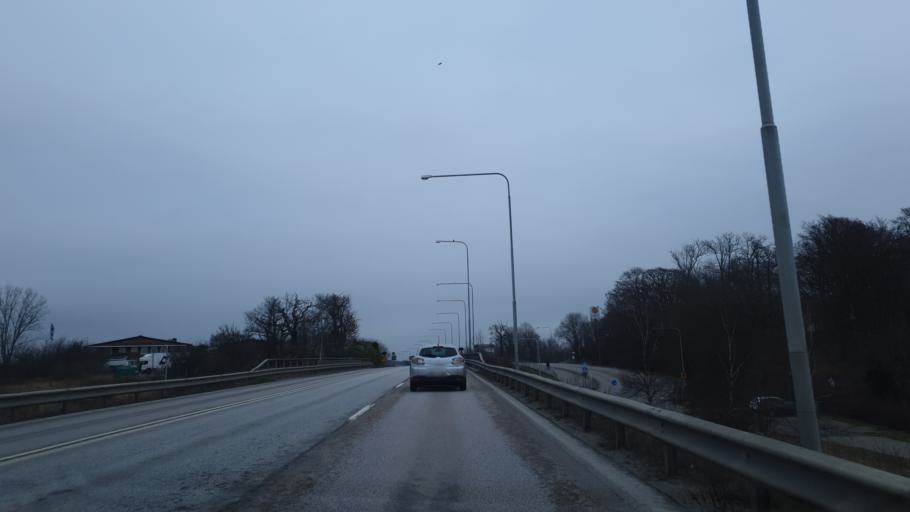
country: SE
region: Blekinge
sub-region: Karlskrona Kommun
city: Karlskrona
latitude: 56.1917
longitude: 15.6252
